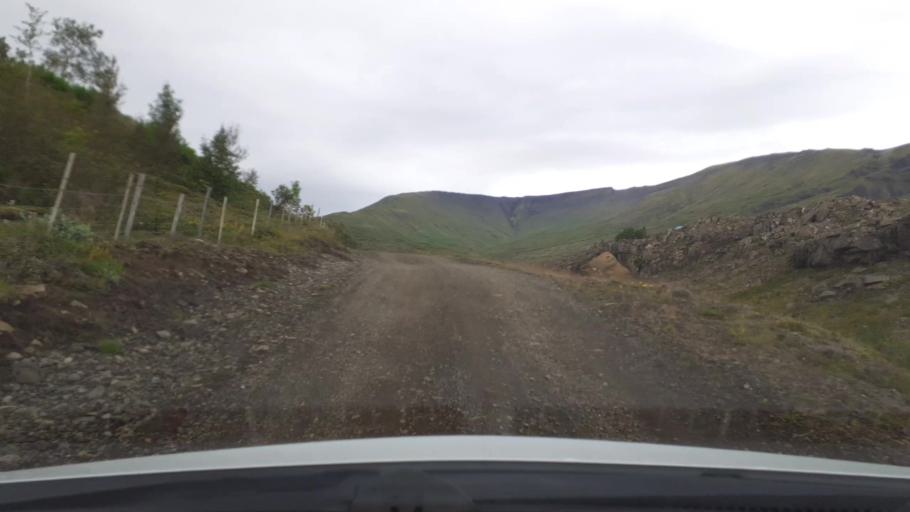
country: IS
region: Capital Region
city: Mosfellsbaer
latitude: 64.2851
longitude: -21.4626
